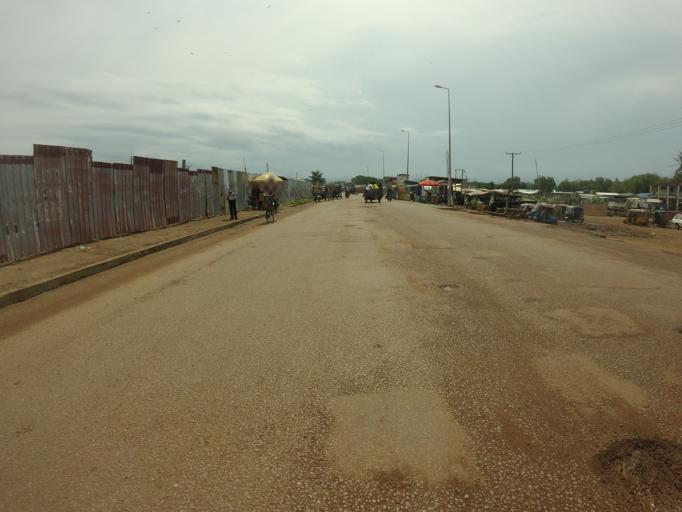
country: GH
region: Upper East
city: Bolgatanga
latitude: 10.7847
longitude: -0.8461
